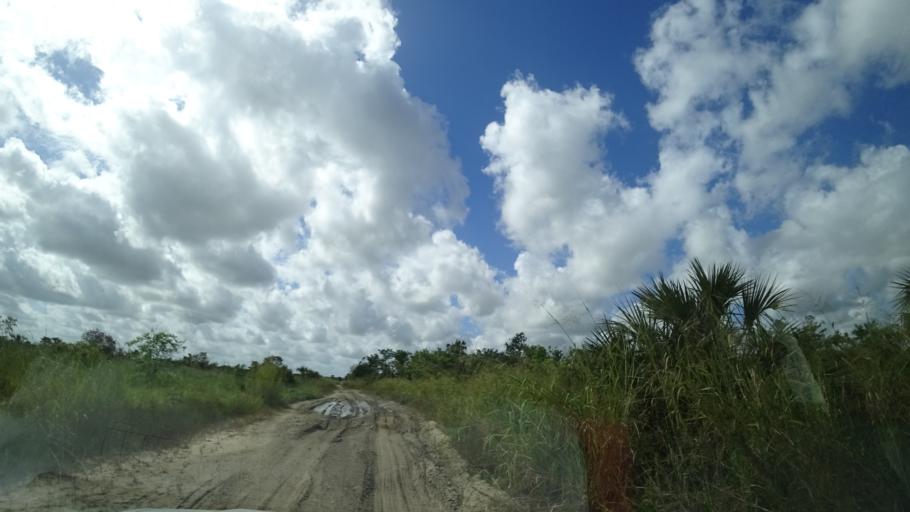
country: MZ
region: Sofala
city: Dondo
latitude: -19.3873
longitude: 34.5839
